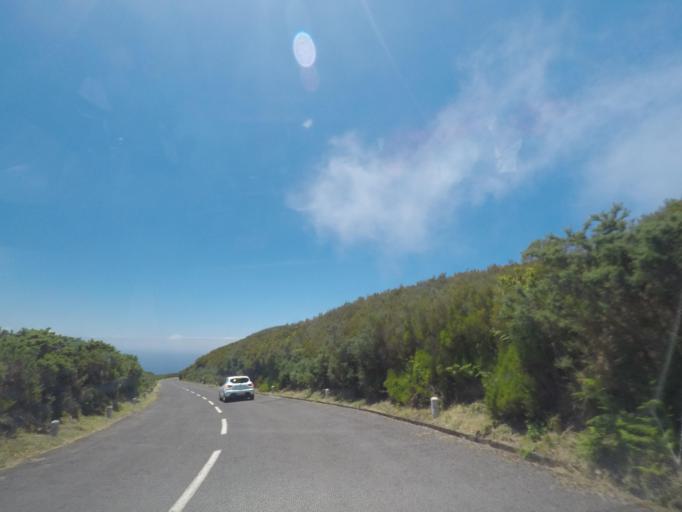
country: PT
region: Madeira
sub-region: Porto Moniz
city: Porto Moniz
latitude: 32.8071
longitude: -17.1930
